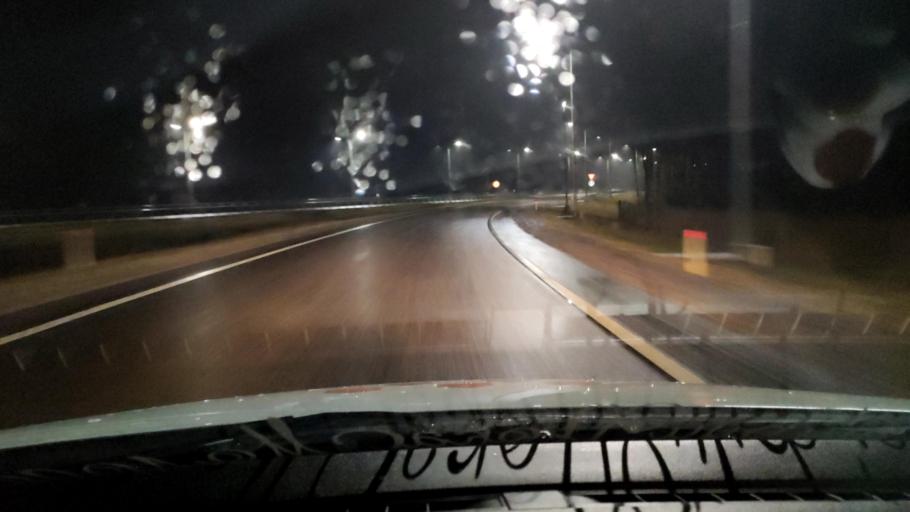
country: RU
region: Voronezj
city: Podgornoye
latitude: 51.8376
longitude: 39.2196
